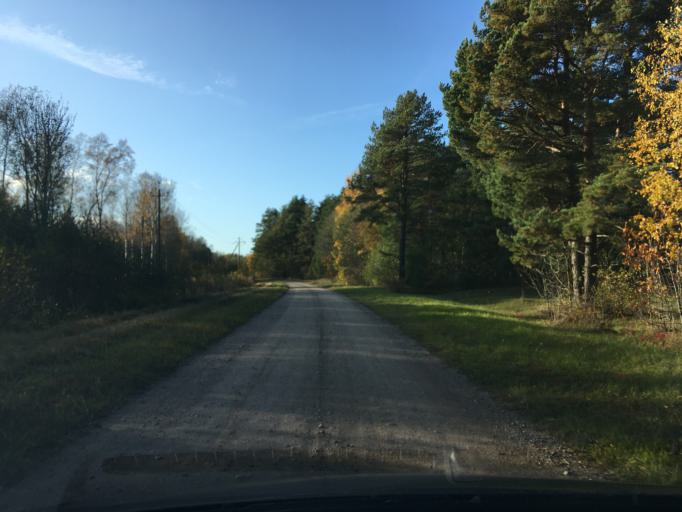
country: EE
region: Laeaene
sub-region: Lihula vald
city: Lihula
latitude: 58.5677
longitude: 23.7616
